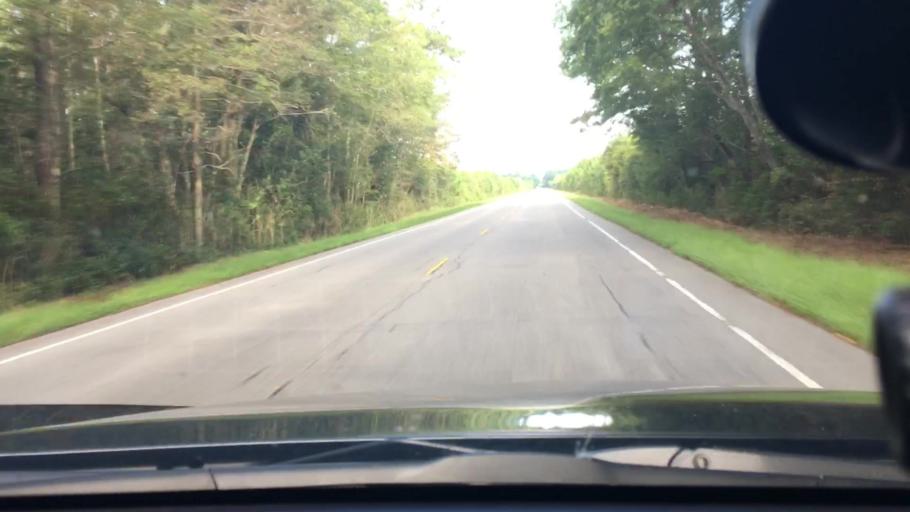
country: US
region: North Carolina
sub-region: Edgecombe County
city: Pinetops
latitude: 35.7687
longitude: -77.5681
